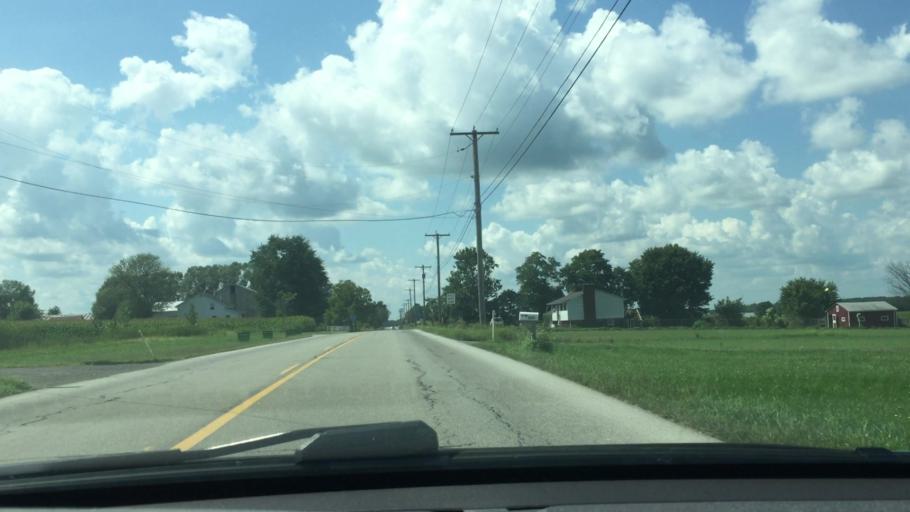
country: US
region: Pennsylvania
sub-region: Lawrence County
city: New Wilmington
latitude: 41.1203
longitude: -80.3698
